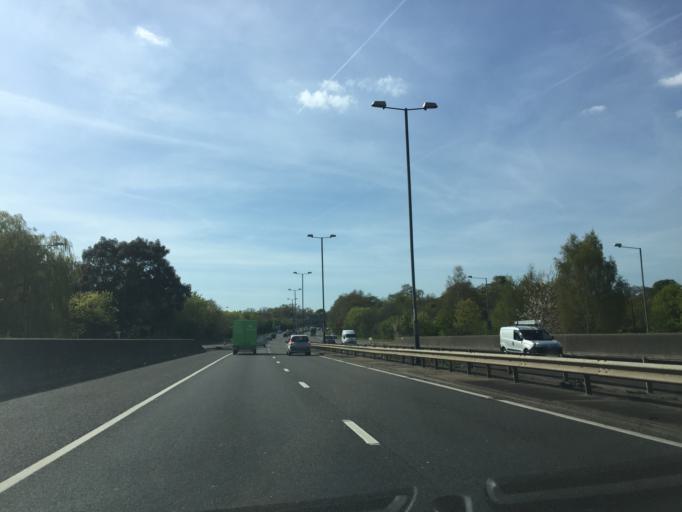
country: GB
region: England
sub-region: Greater London
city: Sidcup
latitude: 51.4138
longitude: 0.1098
